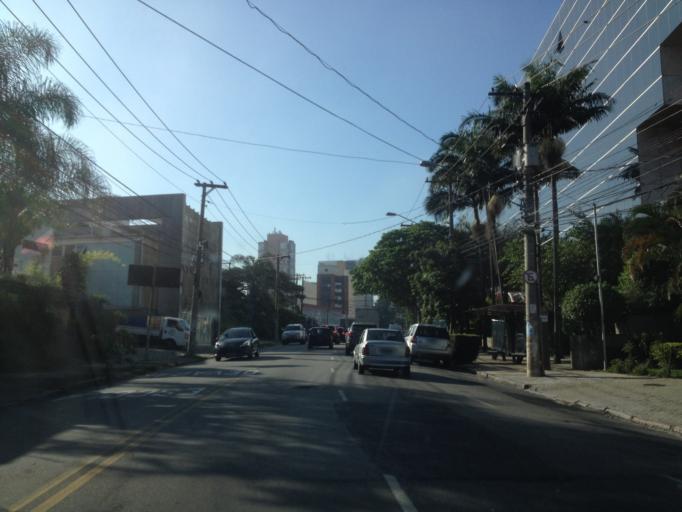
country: BR
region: Sao Paulo
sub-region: Sao Paulo
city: Sao Paulo
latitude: -23.5602
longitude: -46.6947
